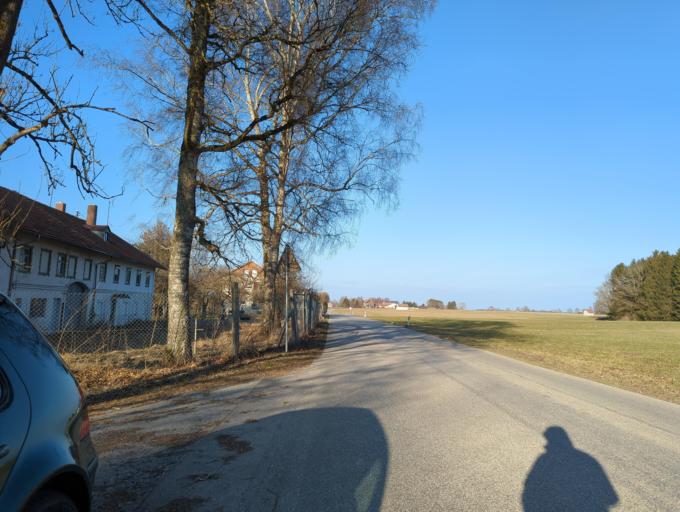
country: DE
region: Bavaria
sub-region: Swabia
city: Bad Worishofen
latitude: 47.9898
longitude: 10.5865
